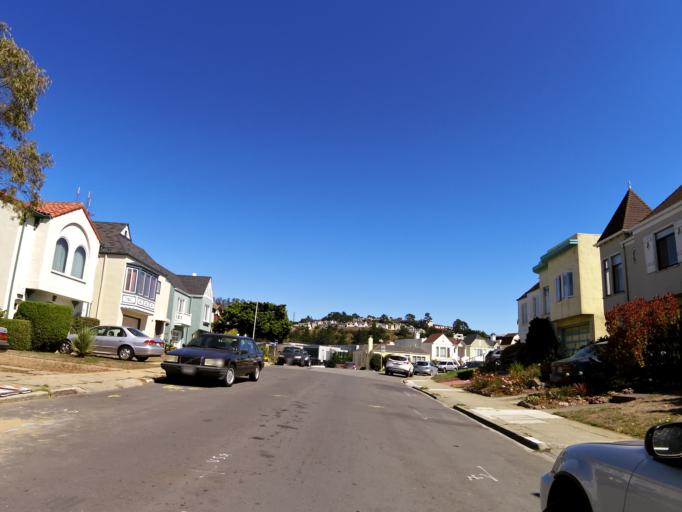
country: US
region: California
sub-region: San Mateo County
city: Daly City
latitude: 37.7444
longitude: -122.4549
